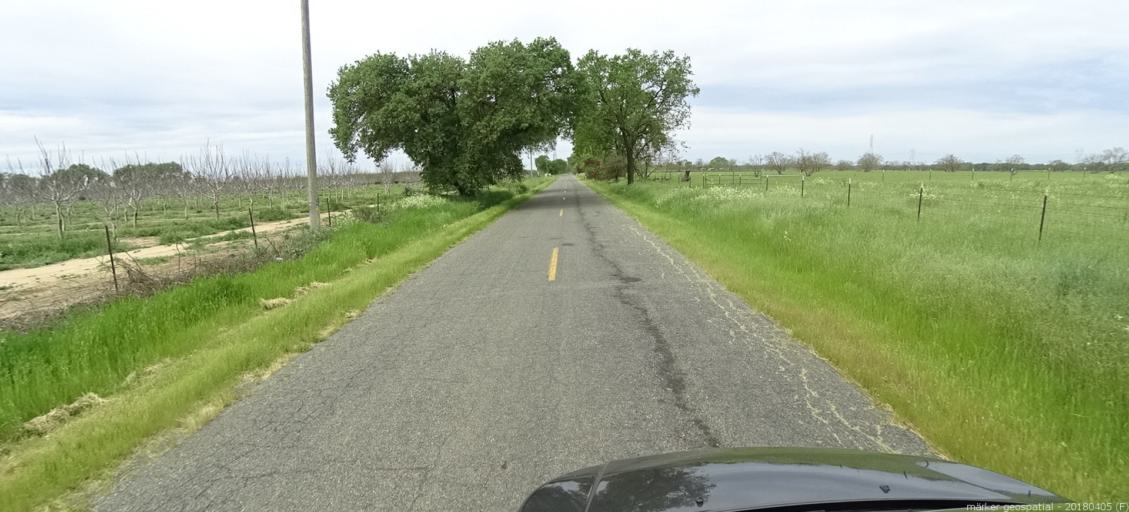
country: US
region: California
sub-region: Sacramento County
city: Galt
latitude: 38.2619
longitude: -121.3532
